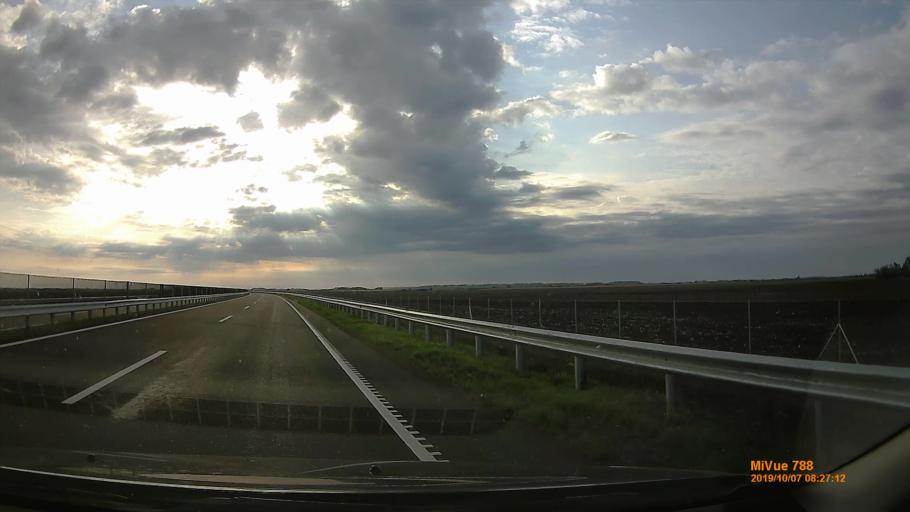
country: HU
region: Jasz-Nagykun-Szolnok
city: Ocsod
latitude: 46.8166
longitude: 20.3796
